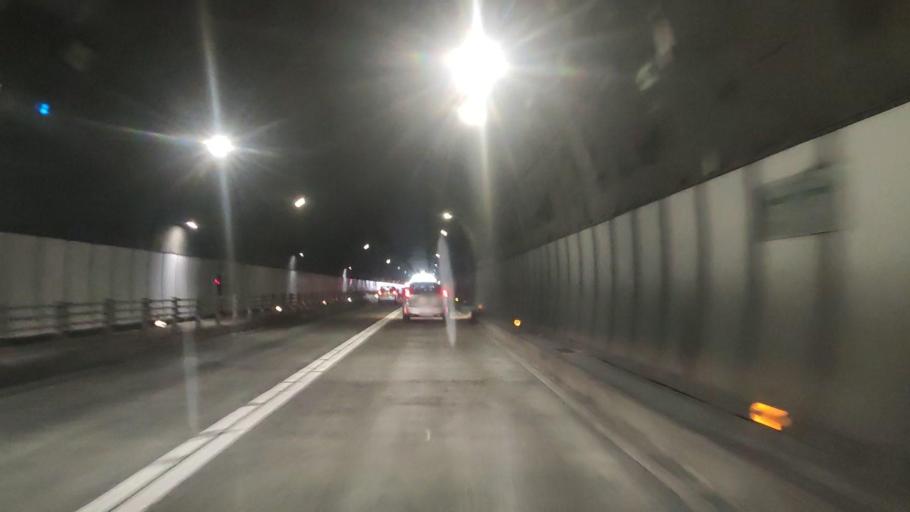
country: JP
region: Yamaguchi
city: Shimonoseki
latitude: 33.9712
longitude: 130.9436
